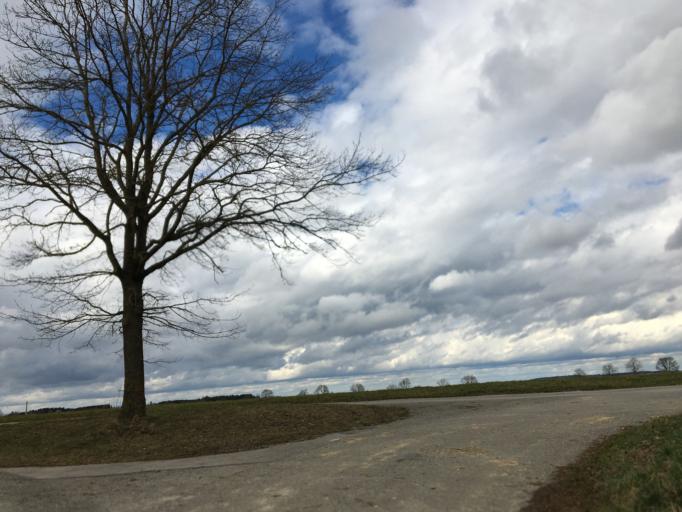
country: DE
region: Bavaria
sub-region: Upper Bavaria
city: Fuerstenfeldbruck
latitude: 48.1888
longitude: 11.2161
